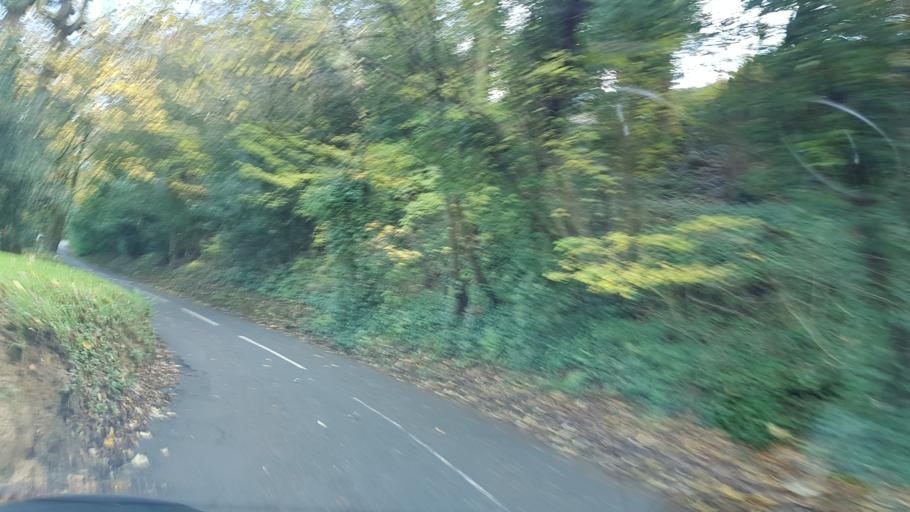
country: GB
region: England
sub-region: Surrey
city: Seale
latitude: 51.2224
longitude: -0.7168
